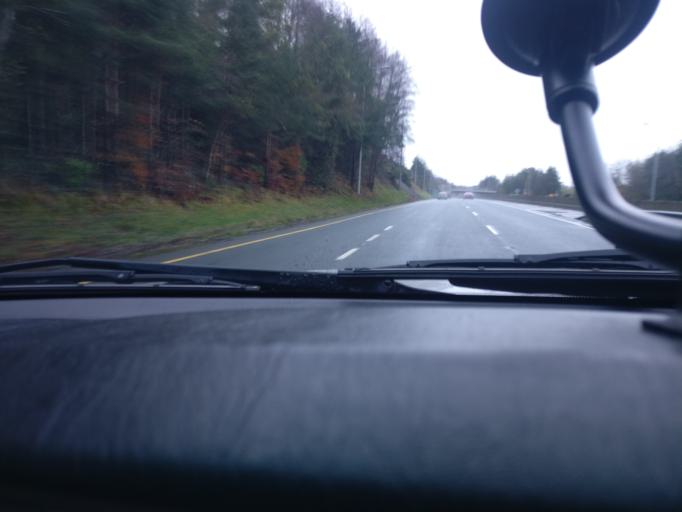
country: IE
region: Leinster
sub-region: An Iarmhi
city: Athlone
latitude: 53.4204
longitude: -7.9814
